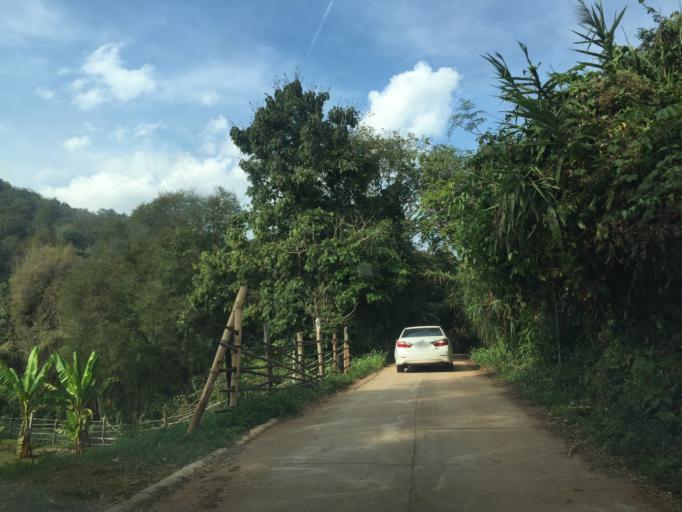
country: TH
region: Chiang Mai
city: Samoeng
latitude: 18.9937
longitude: 98.7277
